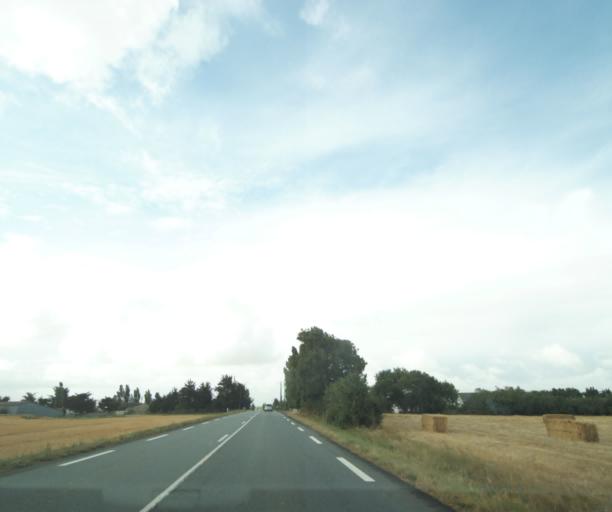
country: FR
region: Poitou-Charentes
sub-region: Departement de la Charente-Maritime
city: Charron
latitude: 46.2968
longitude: -1.0863
